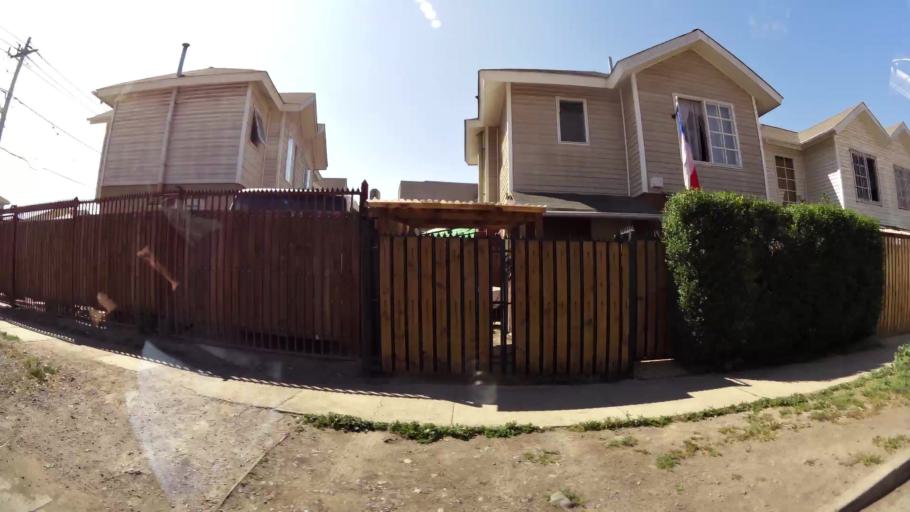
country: CL
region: Santiago Metropolitan
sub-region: Provincia de Chacabuco
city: Chicureo Abajo
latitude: -33.3292
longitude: -70.7488
